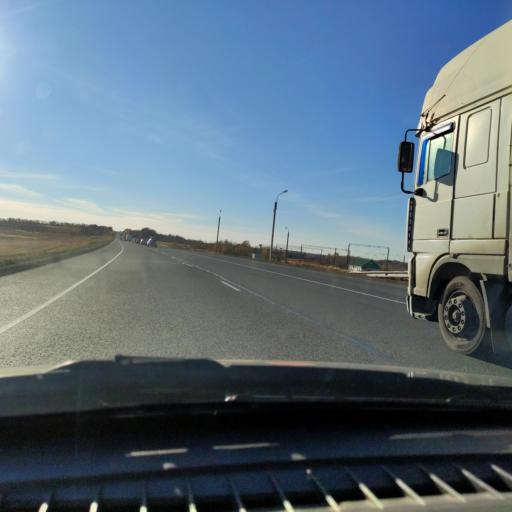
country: RU
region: Samara
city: Obsharovka
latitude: 53.2227
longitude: 48.8677
